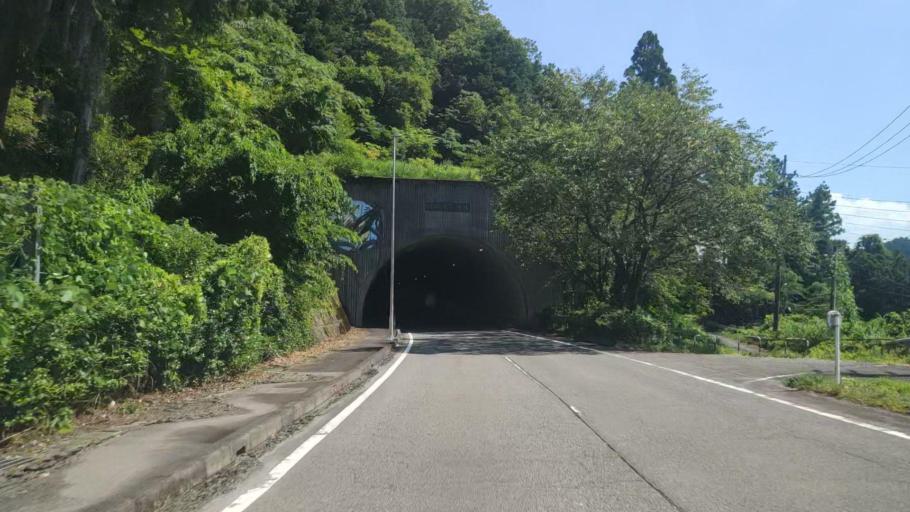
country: JP
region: Gifu
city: Godo
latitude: 35.5605
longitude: 136.6401
